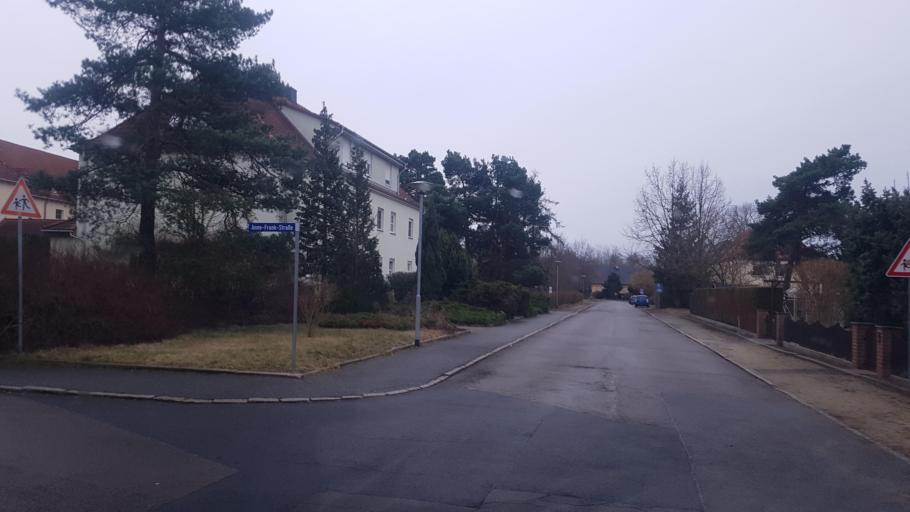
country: DE
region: Brandenburg
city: Schwarzheide
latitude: 51.4748
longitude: 13.8554
